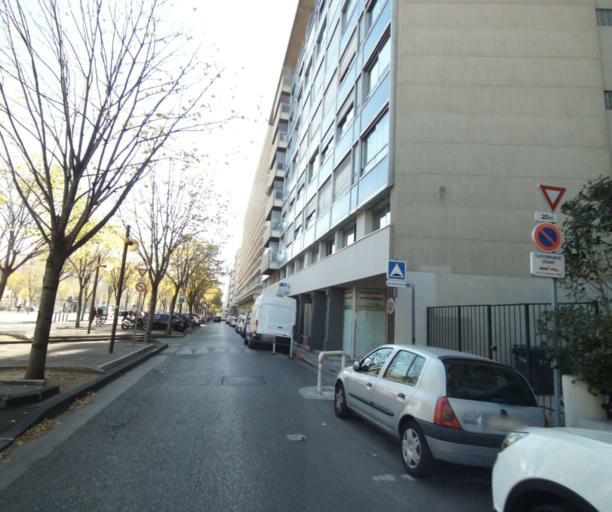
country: FR
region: Provence-Alpes-Cote d'Azur
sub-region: Departement des Bouches-du-Rhone
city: Marseille 08
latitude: 43.2773
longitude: 5.3883
